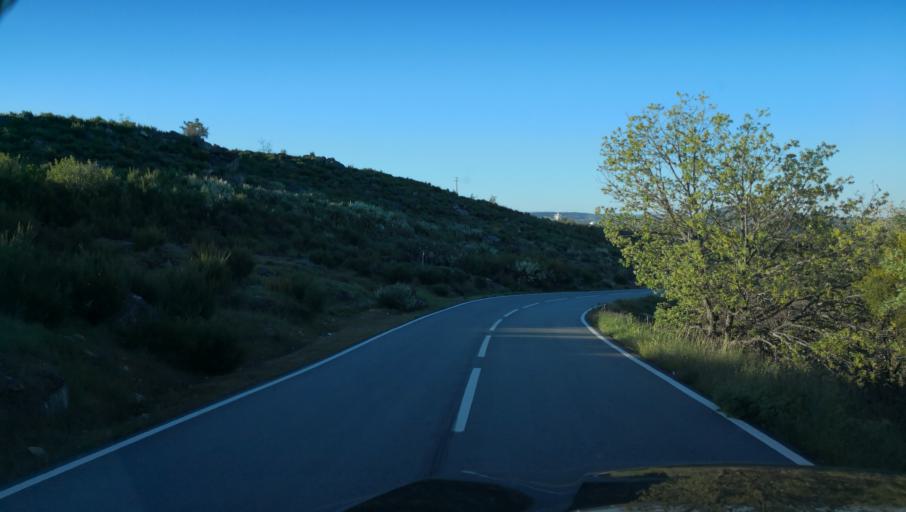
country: PT
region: Vila Real
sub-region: Sabrosa
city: Sabrosa
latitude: 41.3654
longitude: -7.6291
